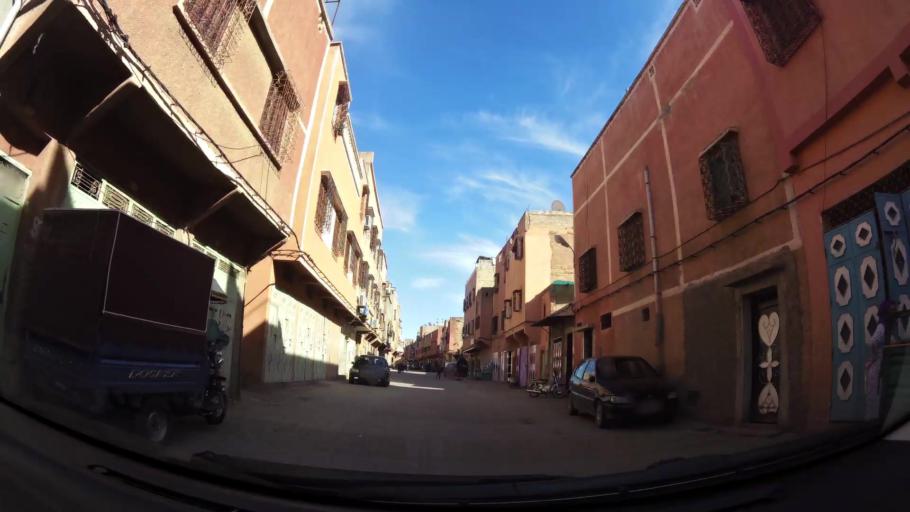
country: MA
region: Marrakech-Tensift-Al Haouz
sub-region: Marrakech
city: Marrakesh
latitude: 31.6155
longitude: -7.9647
